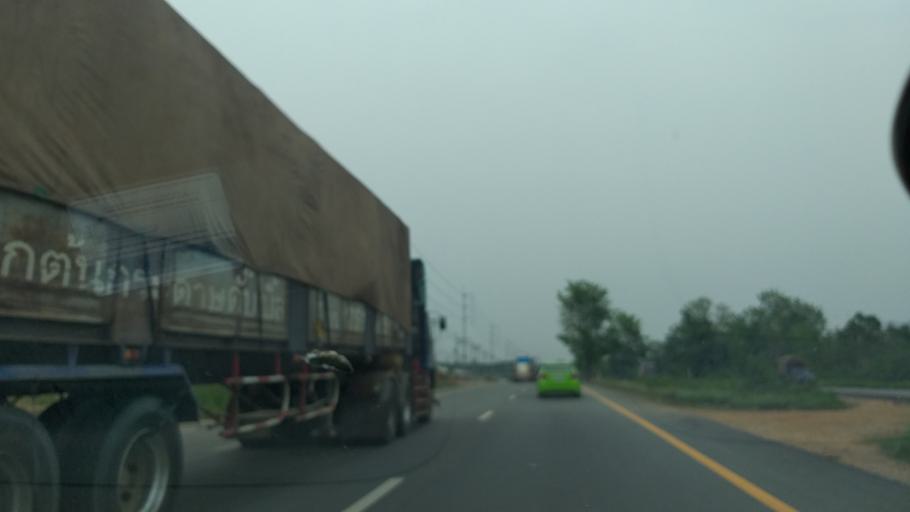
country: TH
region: Chon Buri
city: Ko Chan
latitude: 13.4520
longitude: 101.2836
